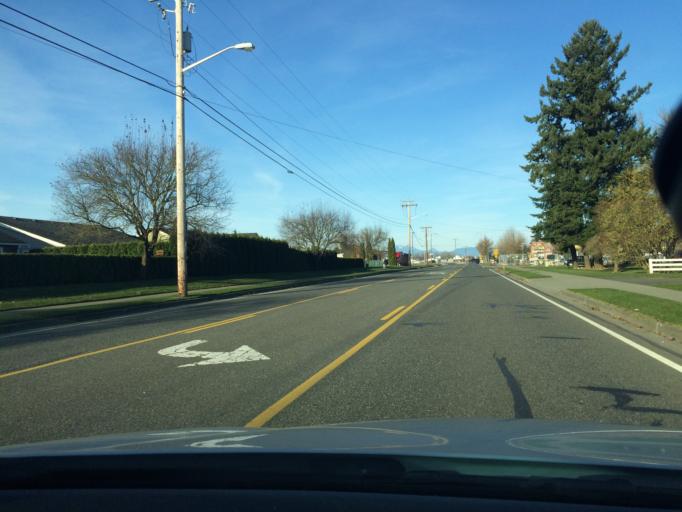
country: US
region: Washington
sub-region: Whatcom County
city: Lynden
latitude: 48.9616
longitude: -122.4412
